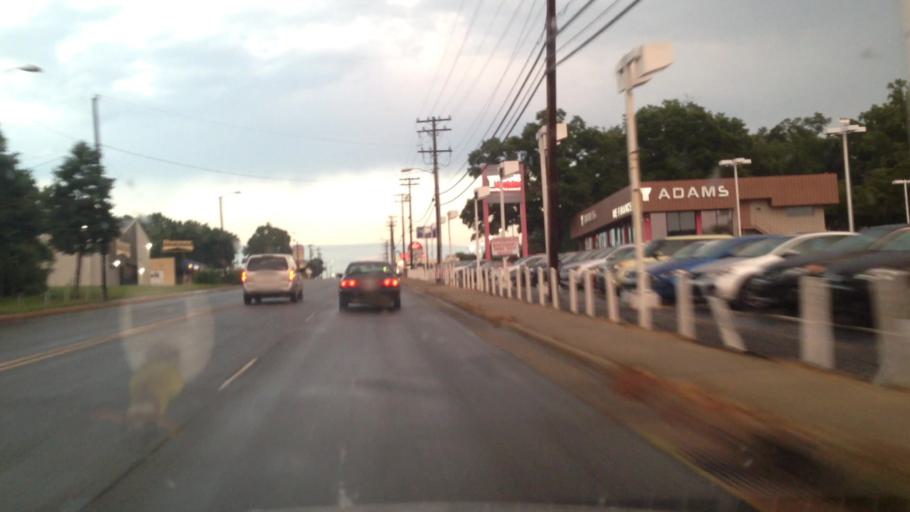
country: US
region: North Carolina
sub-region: Mecklenburg County
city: Pineville
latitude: 35.1456
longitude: -80.8764
